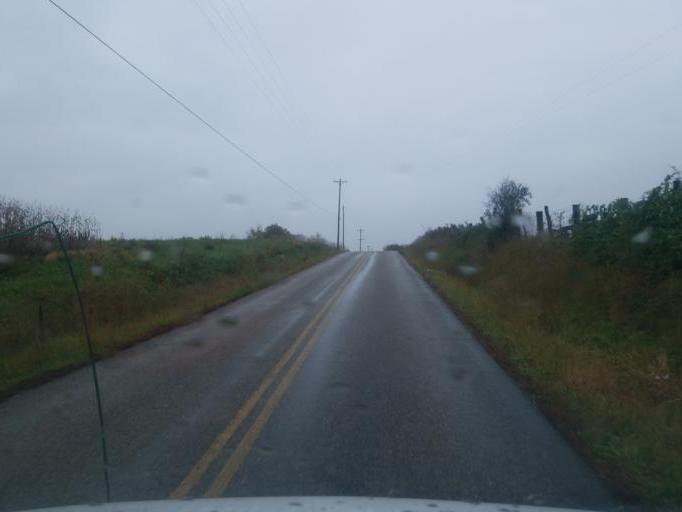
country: US
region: Ohio
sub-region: Washington County
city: Beverly
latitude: 39.4716
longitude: -81.7097
